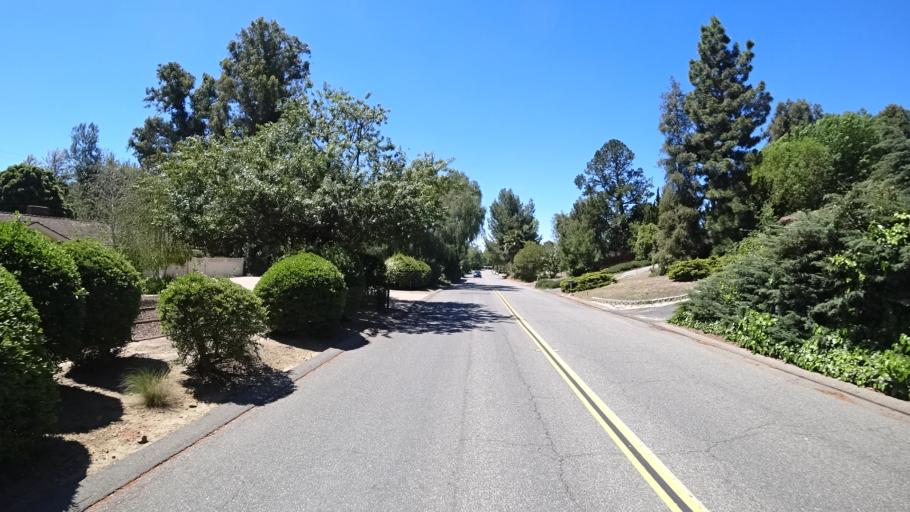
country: US
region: California
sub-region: Ventura County
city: Thousand Oaks
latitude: 34.1920
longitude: -118.8555
